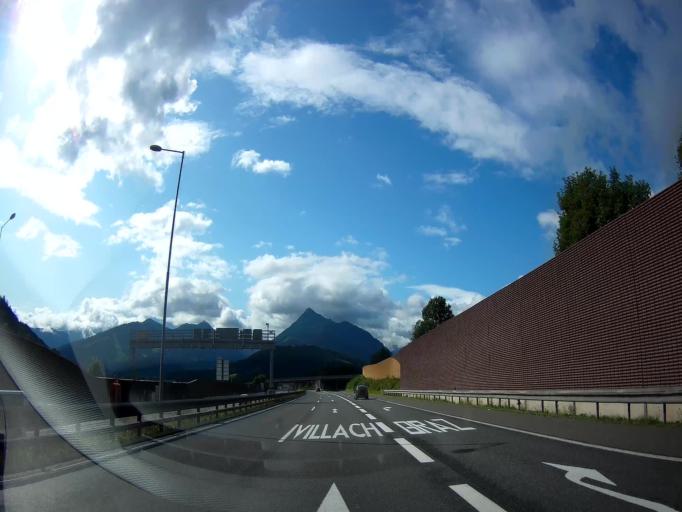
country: AT
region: Salzburg
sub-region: Politischer Bezirk Sankt Johann im Pongau
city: Eben im Pongau
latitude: 47.3993
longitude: 13.3945
